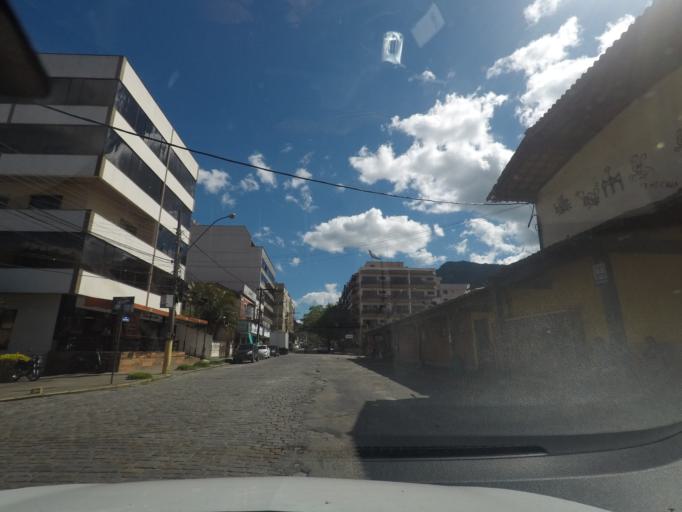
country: BR
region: Rio de Janeiro
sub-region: Teresopolis
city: Teresopolis
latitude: -22.4427
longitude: -42.9785
